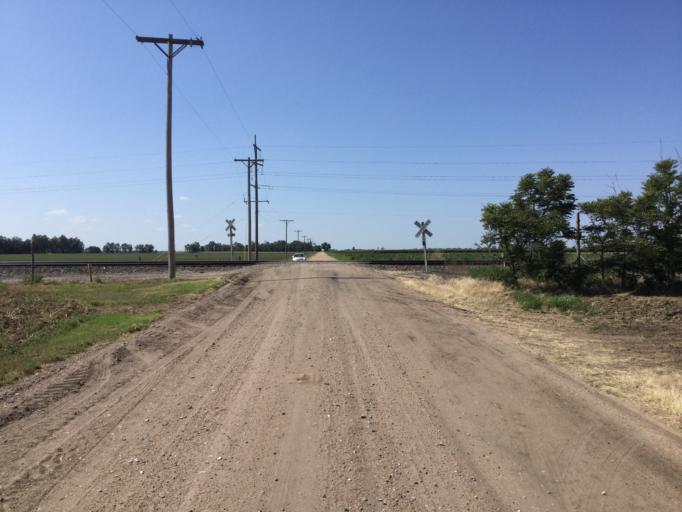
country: US
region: Kansas
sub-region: Harvey County
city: Halstead
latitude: 38.0212
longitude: -97.6472
